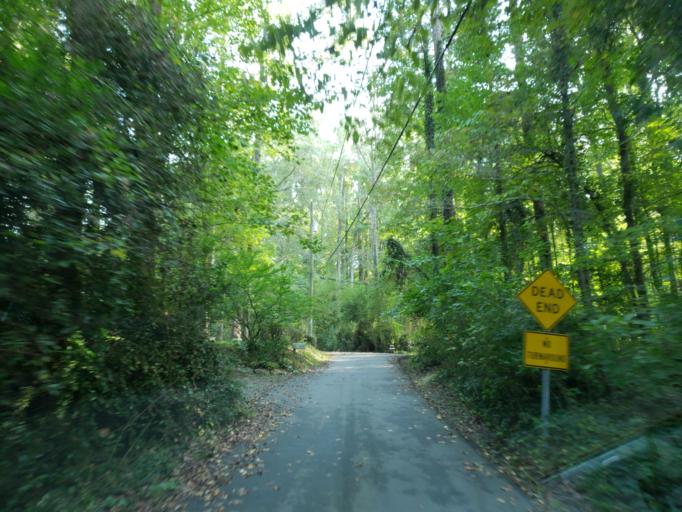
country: US
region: Georgia
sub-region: Fulton County
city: Roswell
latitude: 34.0801
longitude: -84.4174
